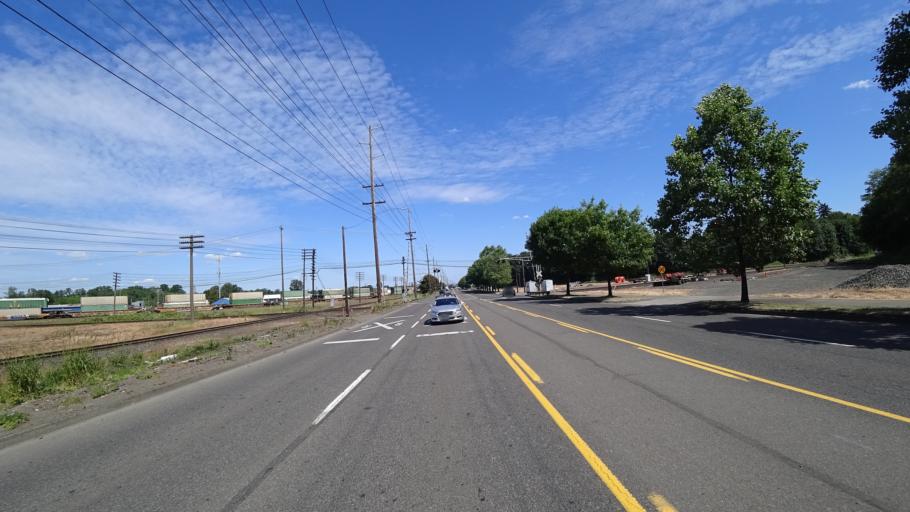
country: US
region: Washington
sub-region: Clark County
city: Vancouver
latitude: 45.5930
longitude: -122.7130
